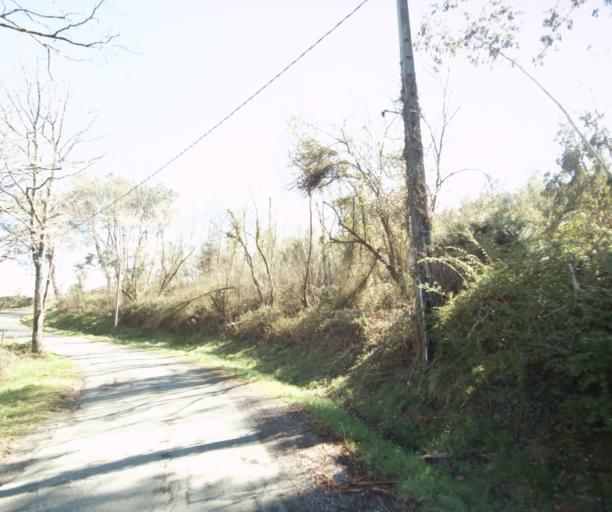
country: FR
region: Aquitaine
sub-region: Departement des Pyrenees-Atlantiques
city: Ascain
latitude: 43.3528
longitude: -1.6560
